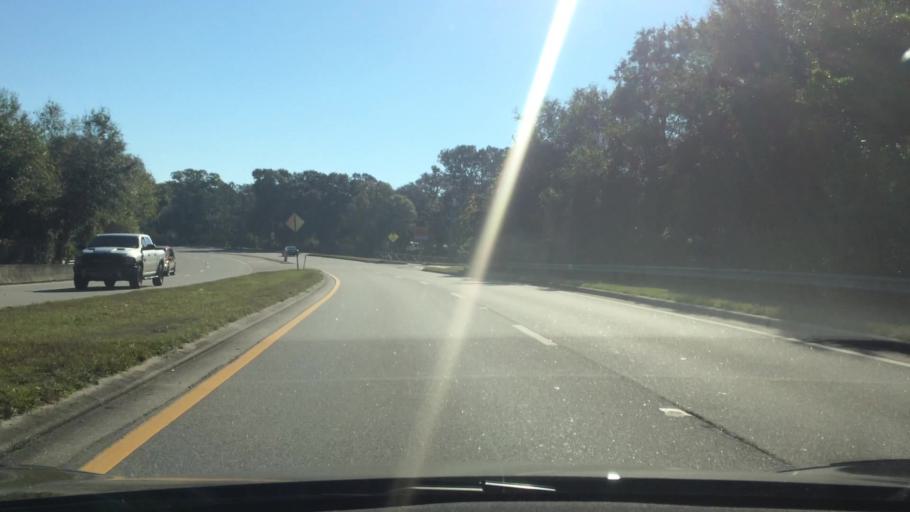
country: US
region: Florida
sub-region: Hillsborough County
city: Lake Magdalene
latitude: 28.0886
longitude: -82.4744
